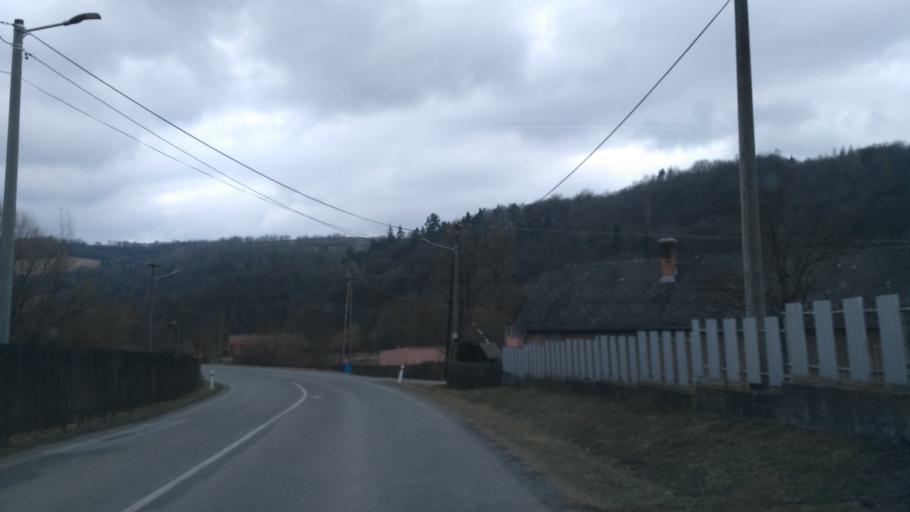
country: SK
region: Presovsky
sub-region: Okres Presov
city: Presov
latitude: 48.9510
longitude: 21.1630
